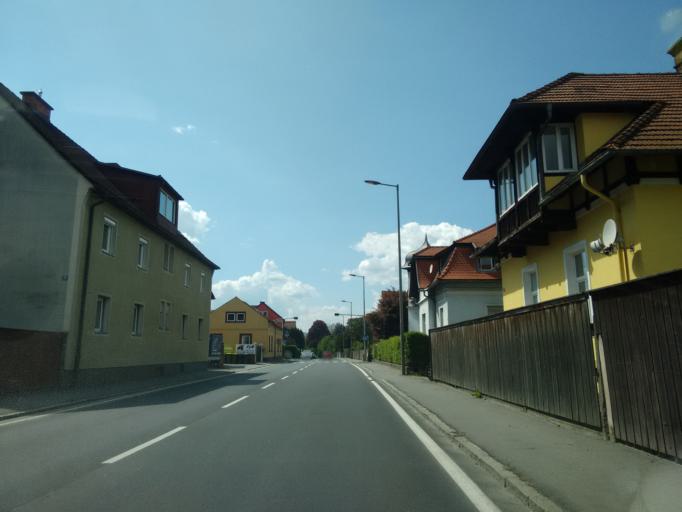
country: AT
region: Styria
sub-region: Politischer Bezirk Bruck-Muerzzuschlag
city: Bruck an der Mur
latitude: 47.4065
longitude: 15.2692
